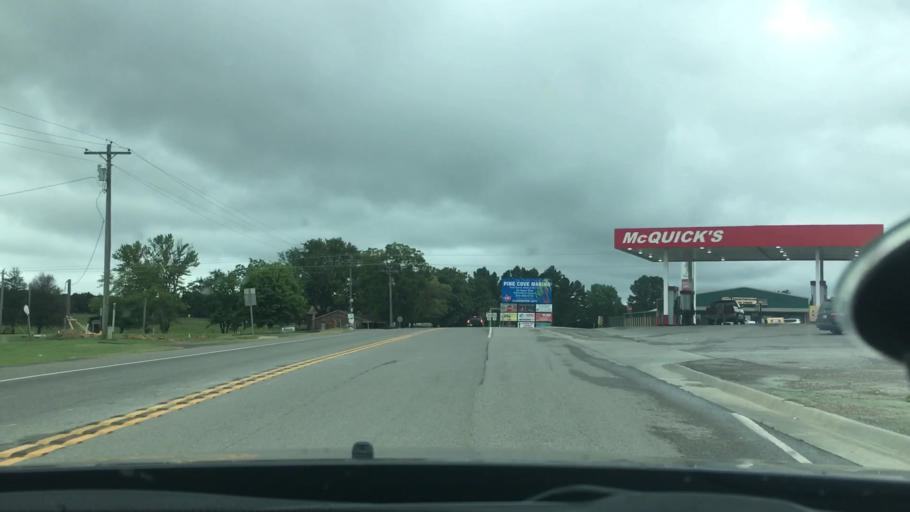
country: US
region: Oklahoma
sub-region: Sequoyah County
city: Vian
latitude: 35.6087
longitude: -94.9763
